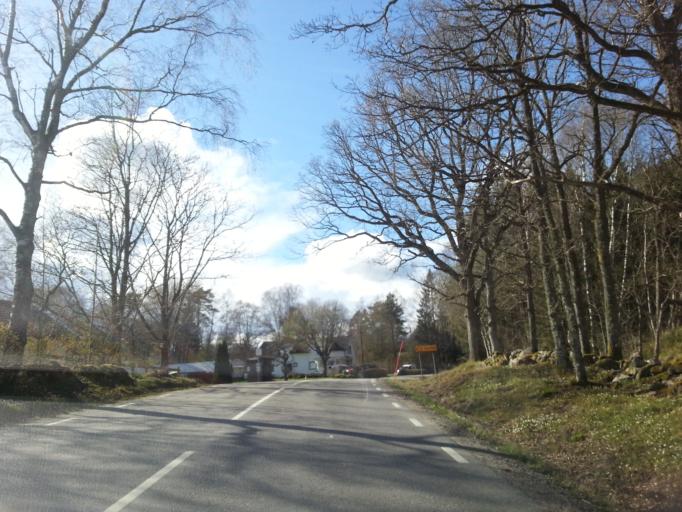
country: SE
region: Vaestra Goetaland
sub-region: Kungalvs Kommun
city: Diserod
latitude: 57.9411
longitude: 12.0152
